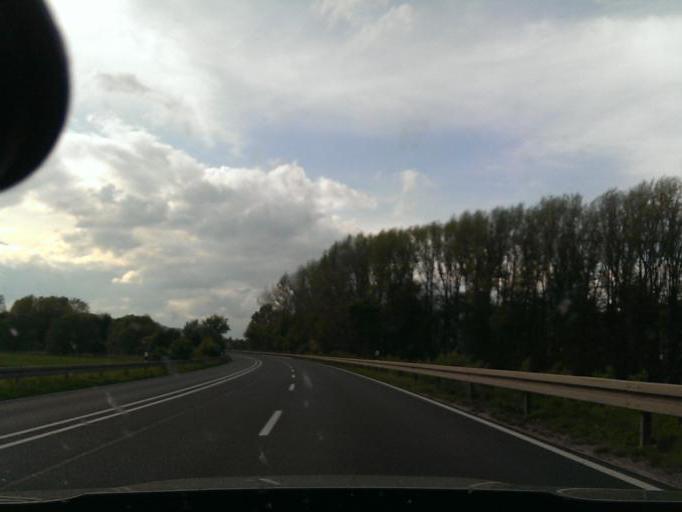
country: DE
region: Lower Saxony
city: Elze
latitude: 52.1034
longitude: 9.7399
